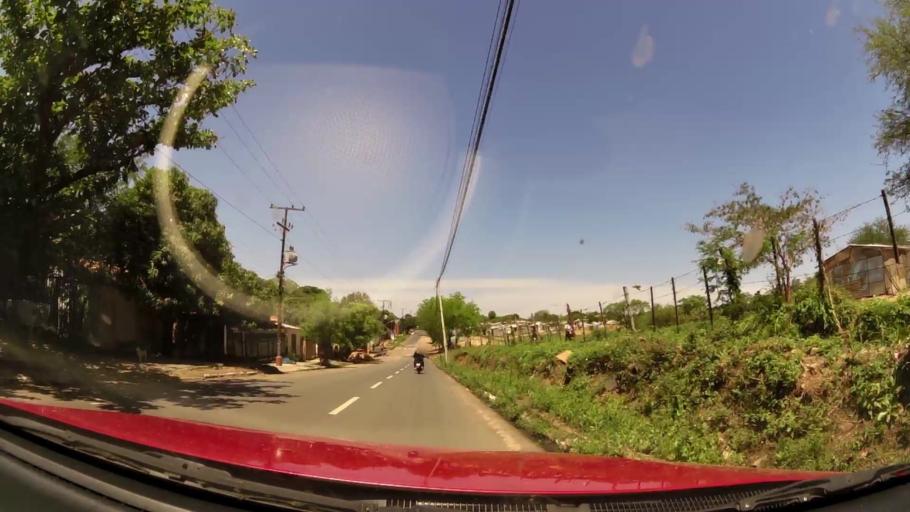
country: PY
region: Central
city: Colonia Mariano Roque Alonso
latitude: -25.2384
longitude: -57.5558
